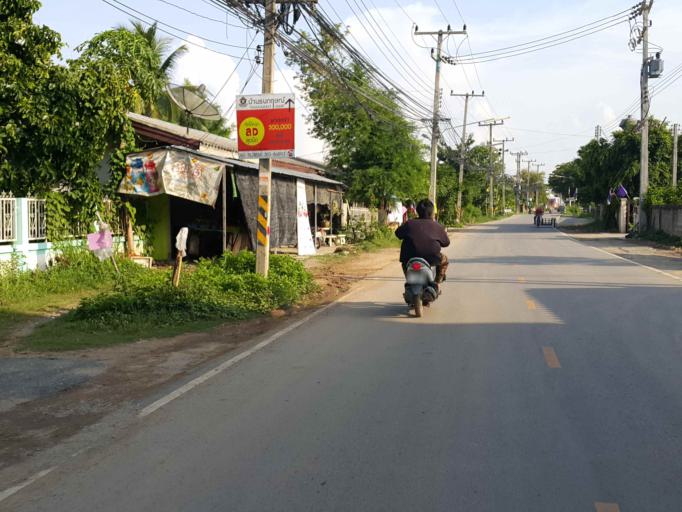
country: TH
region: Chiang Mai
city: San Sai
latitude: 18.8432
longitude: 99.0818
